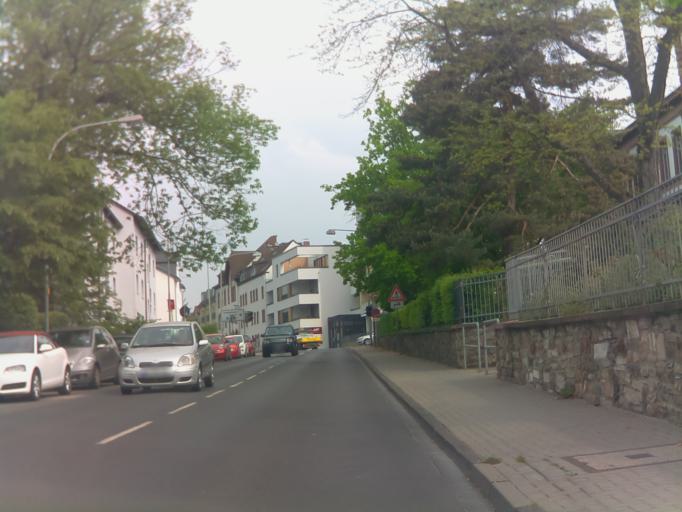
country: DE
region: Hesse
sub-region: Regierungsbezirk Darmstadt
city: Oberursel
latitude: 50.2007
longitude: 8.5765
